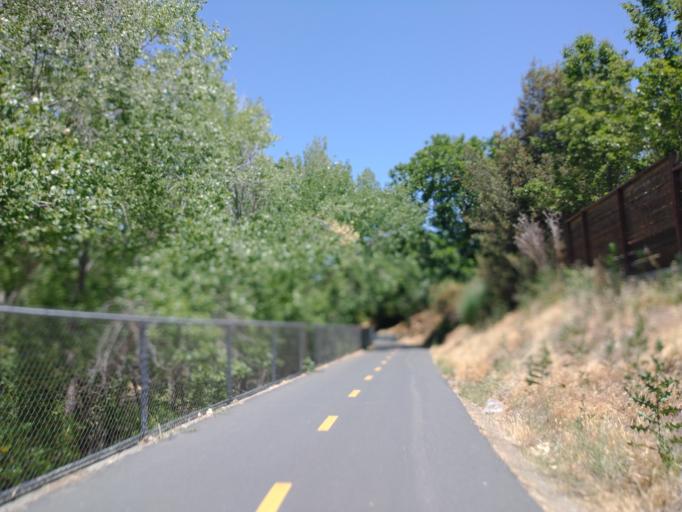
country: US
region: California
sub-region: Santa Clara County
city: Campbell
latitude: 37.2928
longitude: -121.9332
